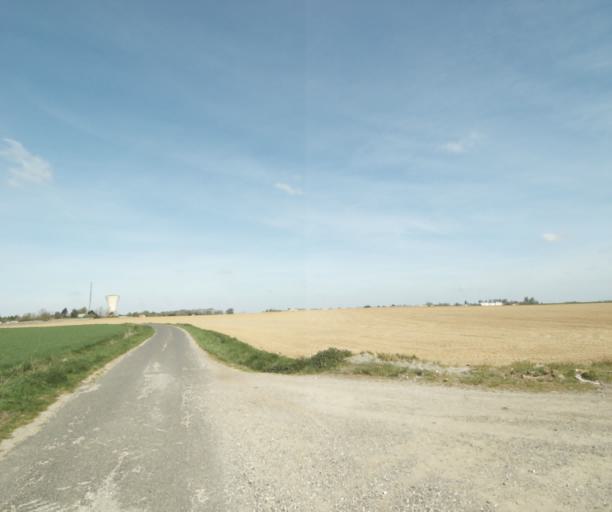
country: FR
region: Ile-de-France
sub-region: Departement de Seine-et-Marne
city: Nangis
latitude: 48.5504
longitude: 3.0325
